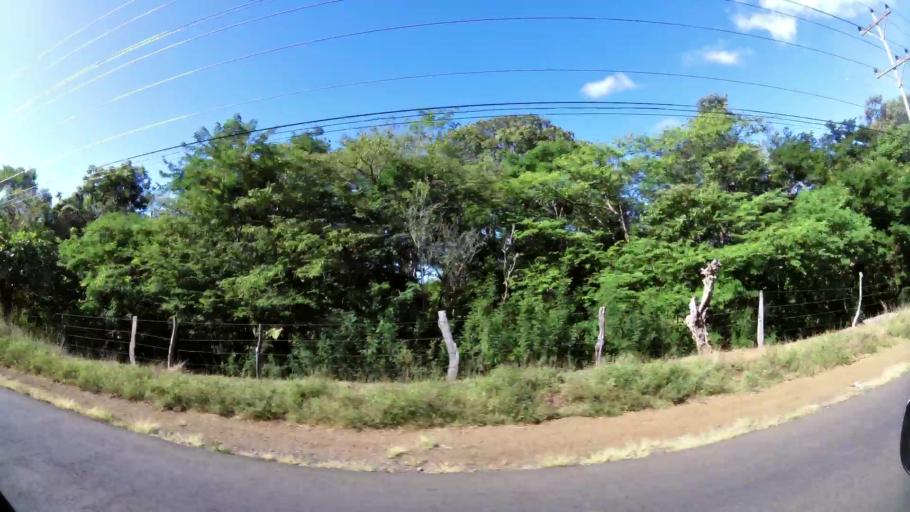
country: CR
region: Guanacaste
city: Sardinal
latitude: 10.3824
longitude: -85.7882
